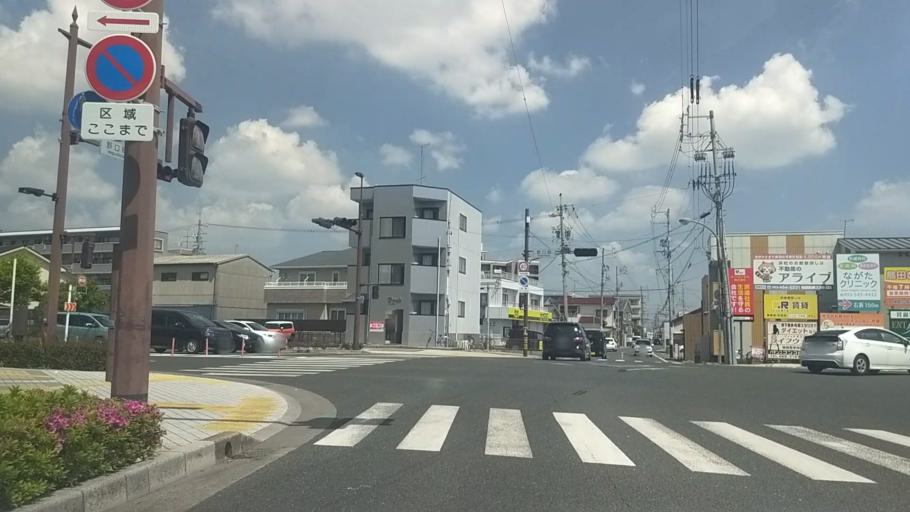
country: JP
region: Shizuoka
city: Hamamatsu
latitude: 34.7130
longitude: 137.7407
